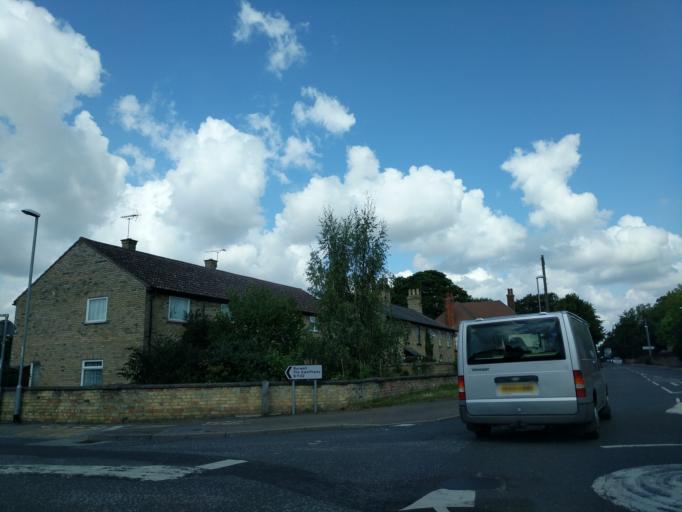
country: GB
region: England
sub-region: Suffolk
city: Exning
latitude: 52.3067
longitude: 0.3846
